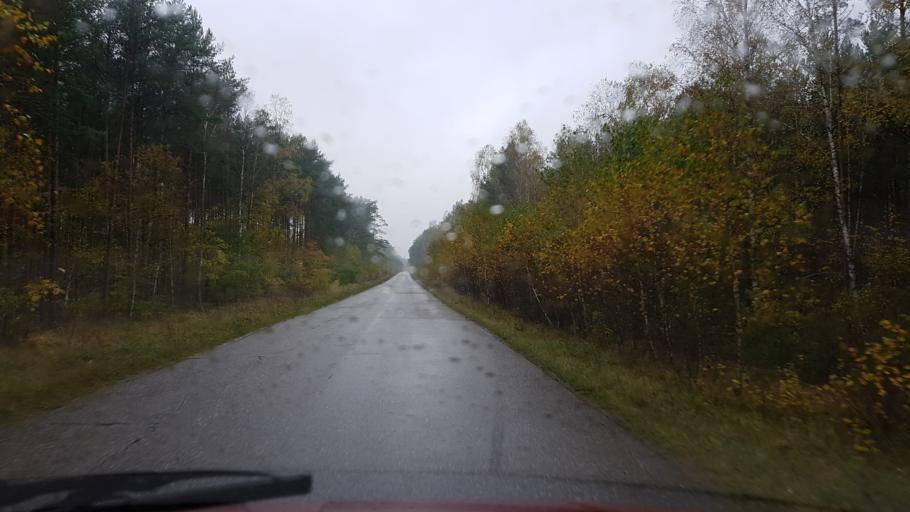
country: PL
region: Greater Poland Voivodeship
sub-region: Powiat zlotowski
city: Tarnowka
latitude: 53.3590
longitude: 16.8095
